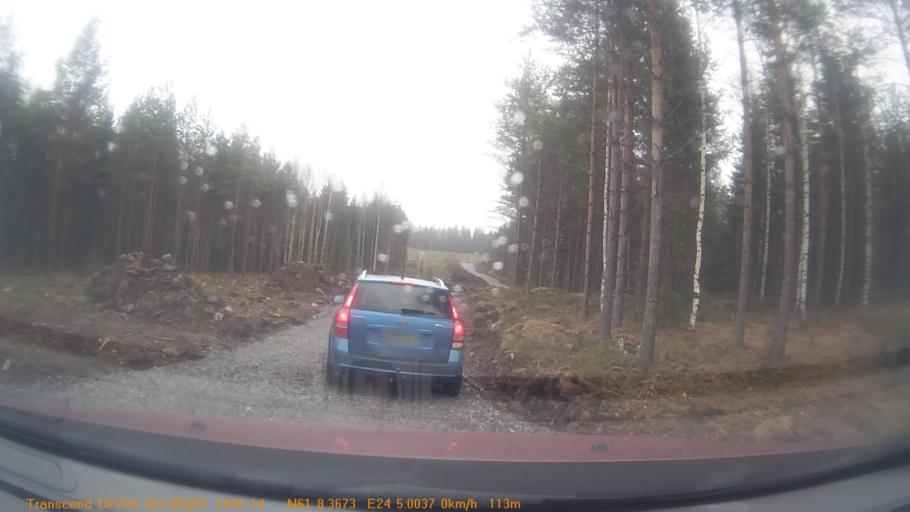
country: FI
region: Haeme
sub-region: Haemeenlinna
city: Kalvola
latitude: 61.1394
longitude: 24.0834
